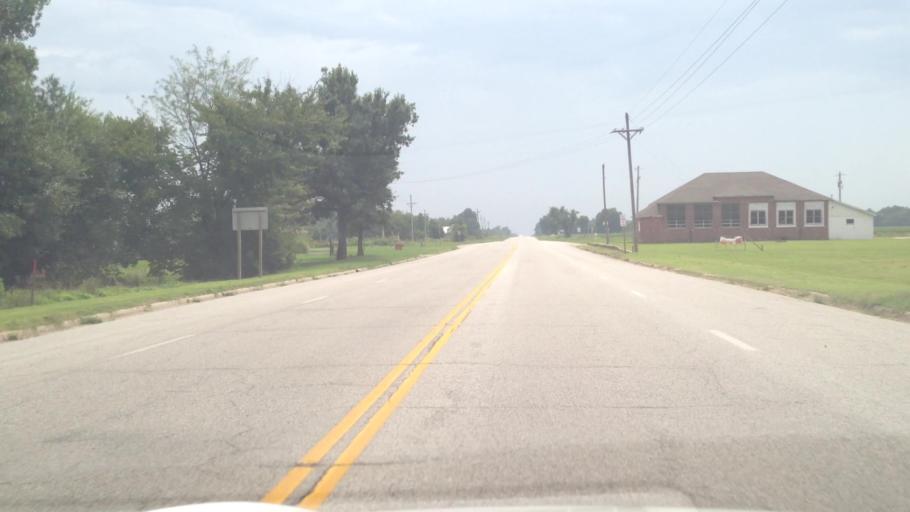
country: US
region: Kansas
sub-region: Cherokee County
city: Galena
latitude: 37.1644
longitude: -94.7044
